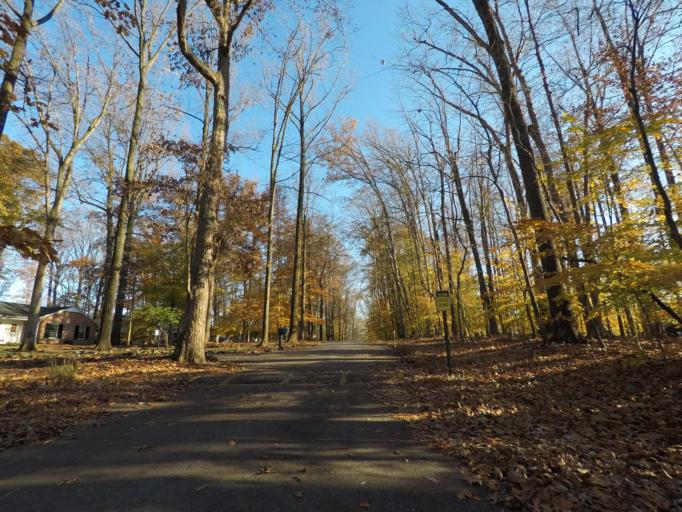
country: US
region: Maryland
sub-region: Howard County
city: Ellicott City
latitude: 39.2861
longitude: -76.7964
